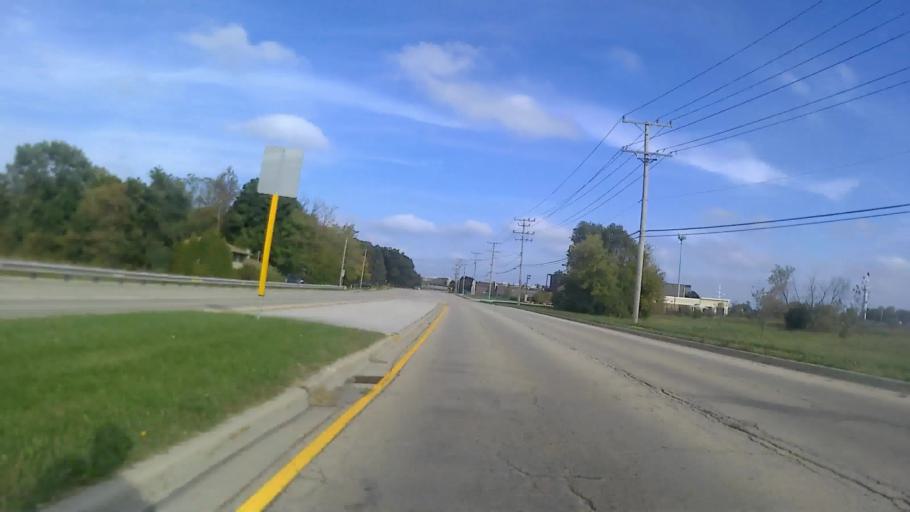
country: US
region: Illinois
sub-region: DuPage County
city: Warrenville
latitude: 41.8067
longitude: -88.1846
